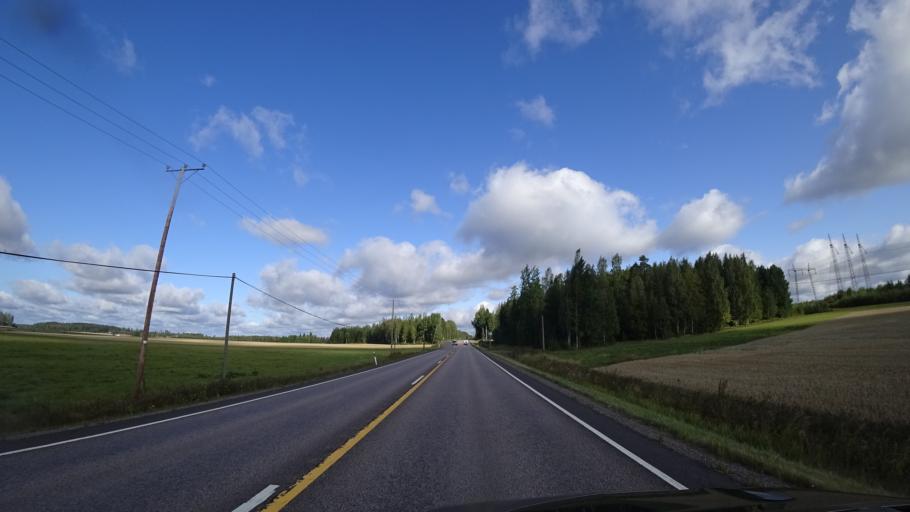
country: FI
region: Uusimaa
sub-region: Helsinki
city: Nurmijaervi
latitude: 60.5022
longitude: 24.9331
